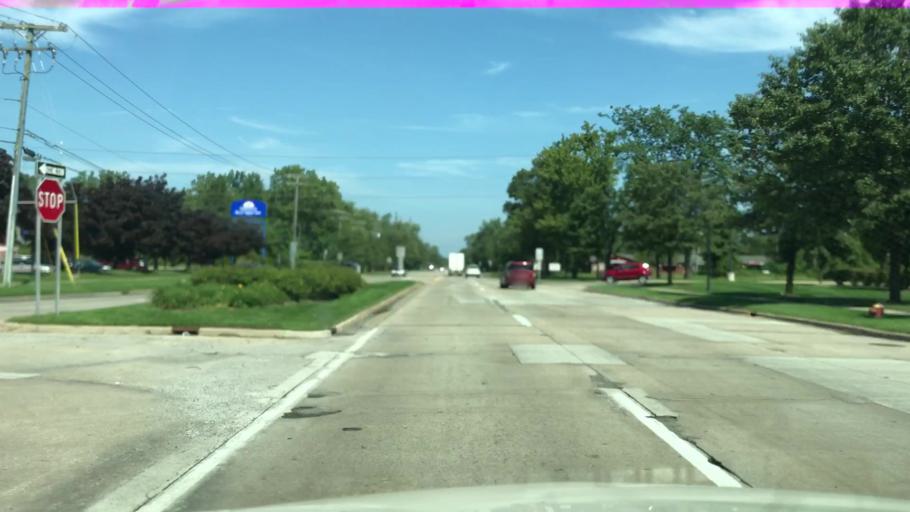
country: US
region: Michigan
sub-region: Wayne County
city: Wayne
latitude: 42.2480
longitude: -83.3476
